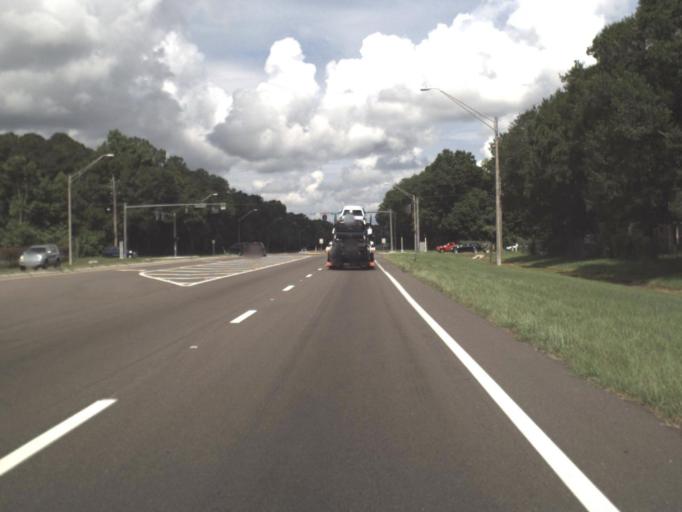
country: US
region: Florida
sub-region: Duval County
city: Jacksonville
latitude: 30.3569
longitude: -81.6999
